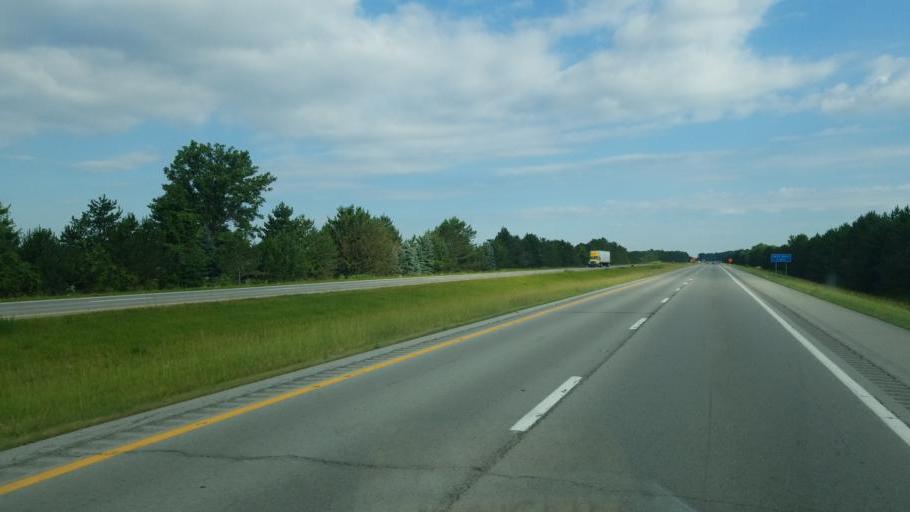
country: US
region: Ohio
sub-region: Wyandot County
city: Carey
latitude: 40.9048
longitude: -83.3471
